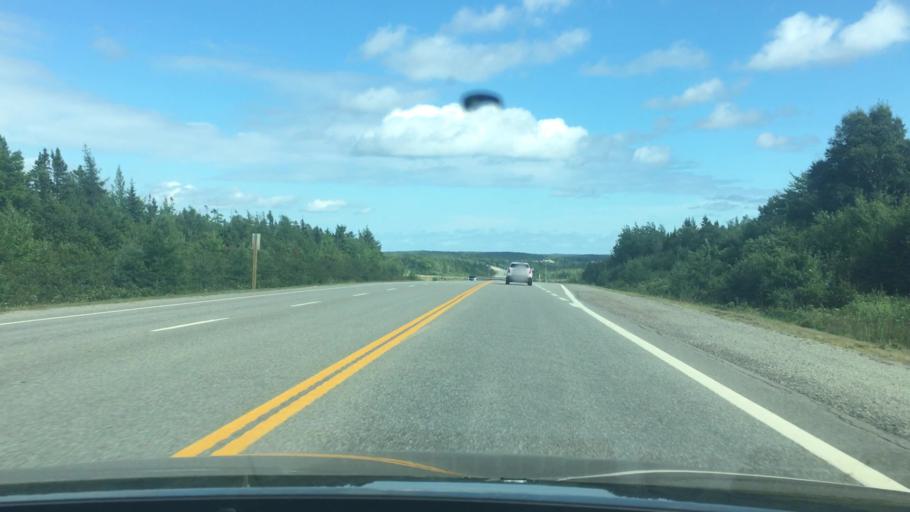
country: CA
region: Nova Scotia
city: Princeville
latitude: 45.6142
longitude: -61.0898
